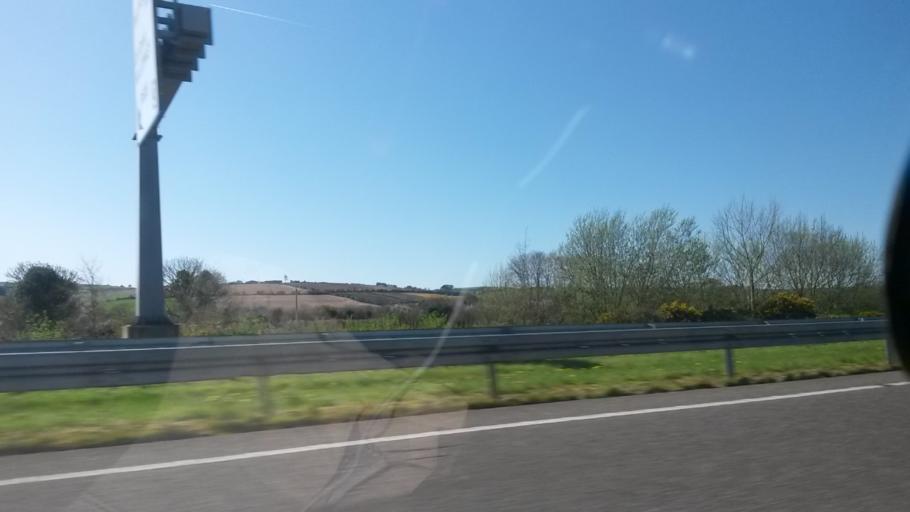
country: IE
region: Munster
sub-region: County Cork
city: Killumney
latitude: 51.8787
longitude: -8.6295
